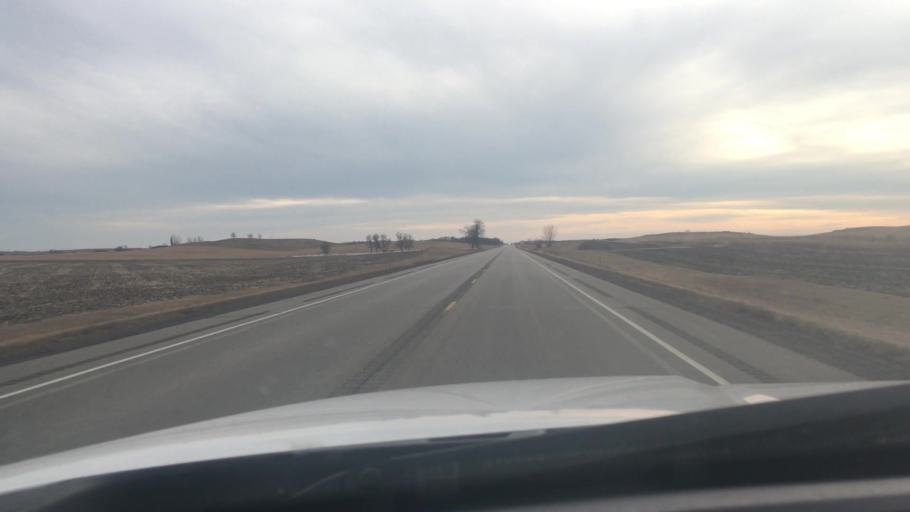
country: US
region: Minnesota
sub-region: Otter Tail County
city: Perham
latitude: 46.3442
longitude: -95.7184
